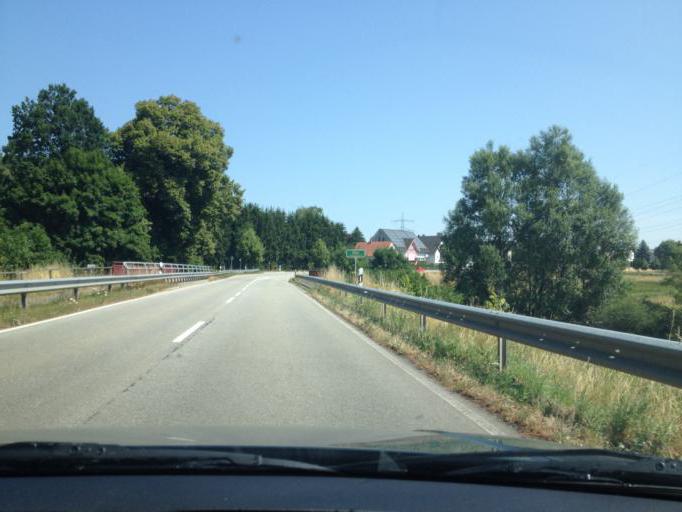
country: DE
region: Rheinland-Pfalz
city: Hutschenhausen
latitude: 49.4155
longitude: 7.4598
